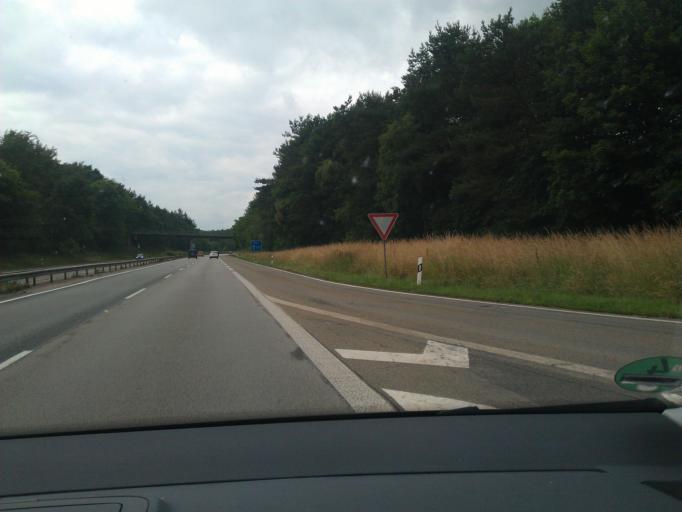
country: DE
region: Rheinland-Pfalz
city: Hutschenhausen
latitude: 49.4433
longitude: 7.4979
